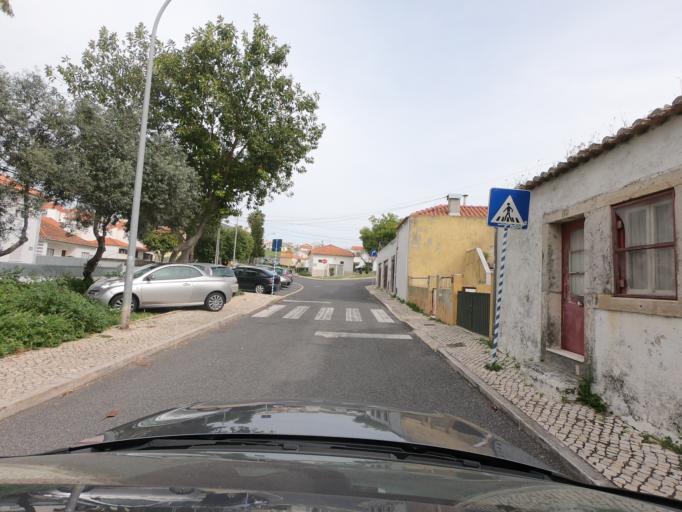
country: PT
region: Lisbon
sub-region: Oeiras
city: Porto Salvo
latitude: 38.7167
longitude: -9.2990
